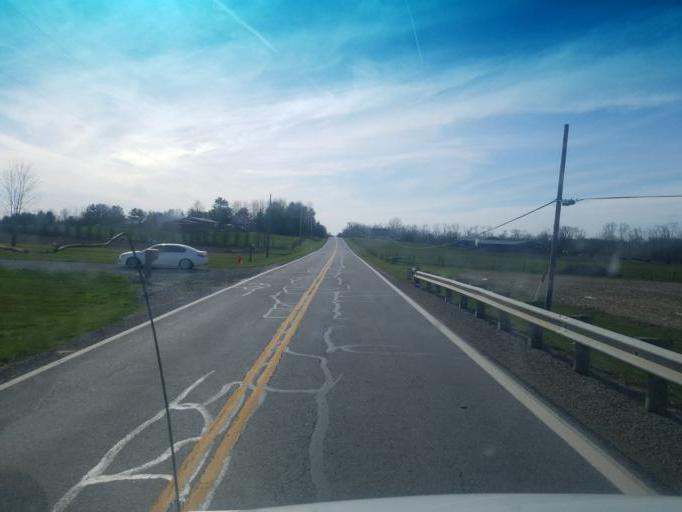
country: US
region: Ohio
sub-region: Champaign County
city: North Lewisburg
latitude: 40.3389
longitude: -83.4737
